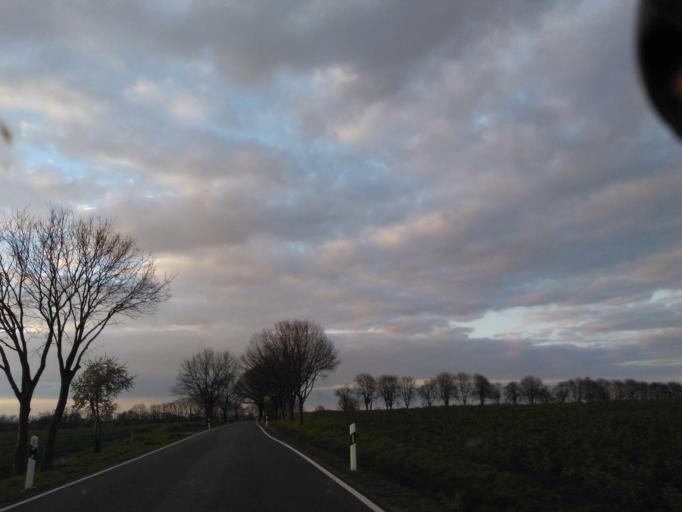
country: DE
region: Brandenburg
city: Buckow
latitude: 52.6266
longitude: 14.0692
